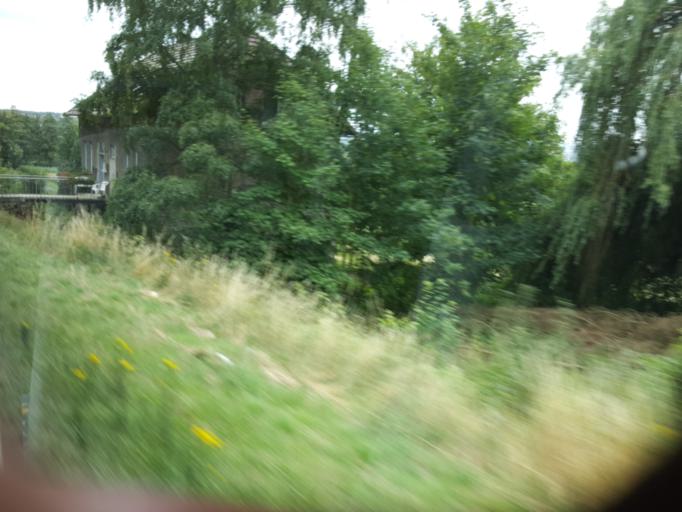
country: DE
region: North Rhine-Westphalia
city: Porta Westfalica
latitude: 52.2445
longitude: 8.8766
